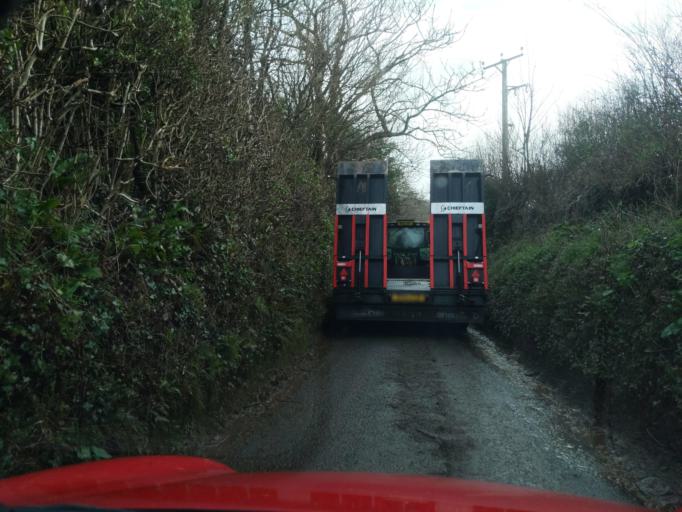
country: GB
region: England
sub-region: Devon
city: Ivybridge
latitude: 50.3561
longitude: -3.9295
